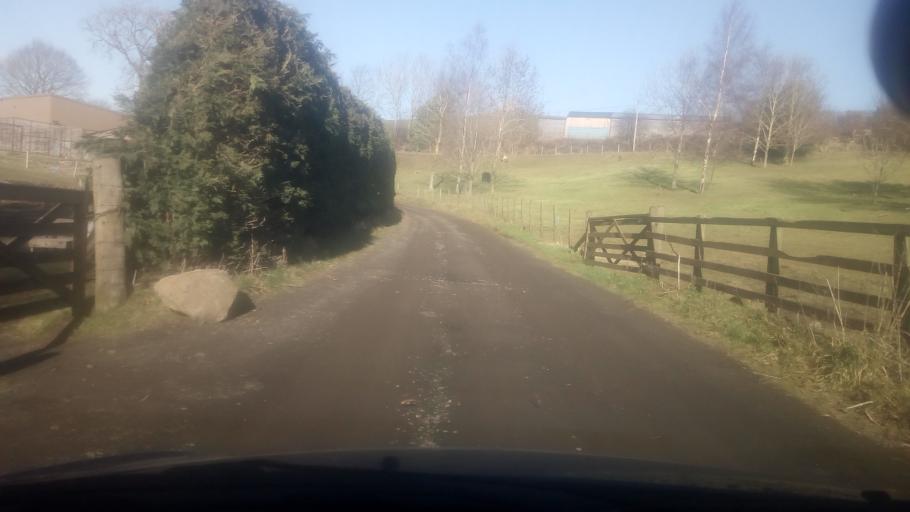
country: GB
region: Scotland
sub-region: The Scottish Borders
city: Jedburgh
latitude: 55.4853
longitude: -2.5355
